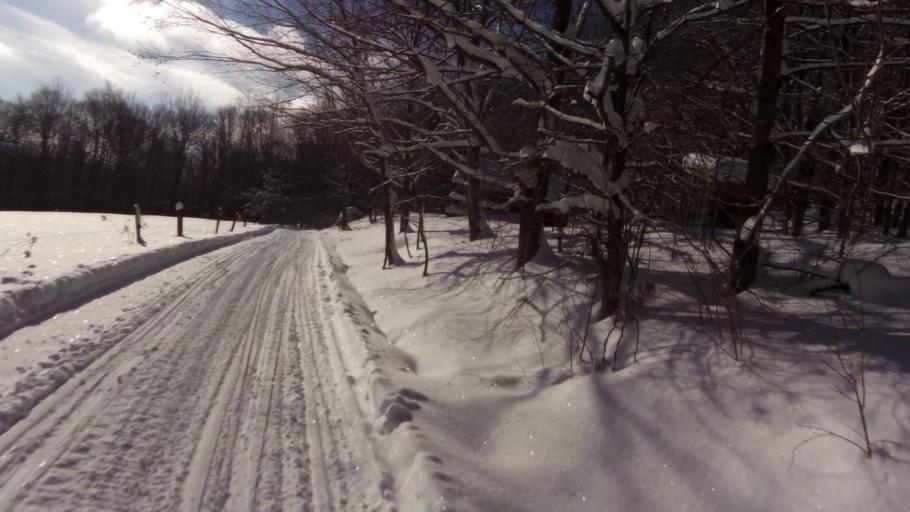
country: US
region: New York
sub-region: Chautauqua County
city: Falconer
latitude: 42.2732
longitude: -79.1206
